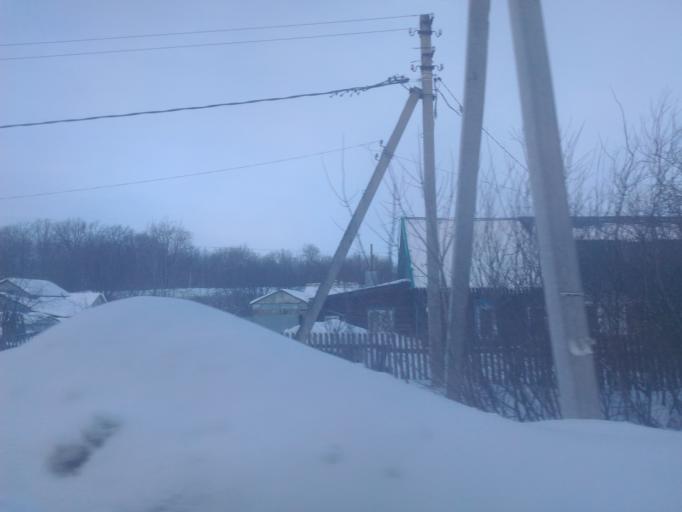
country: RU
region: Ulyanovsk
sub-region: Ulyanovskiy Rayon
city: Ulyanovsk
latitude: 54.3642
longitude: 48.3499
